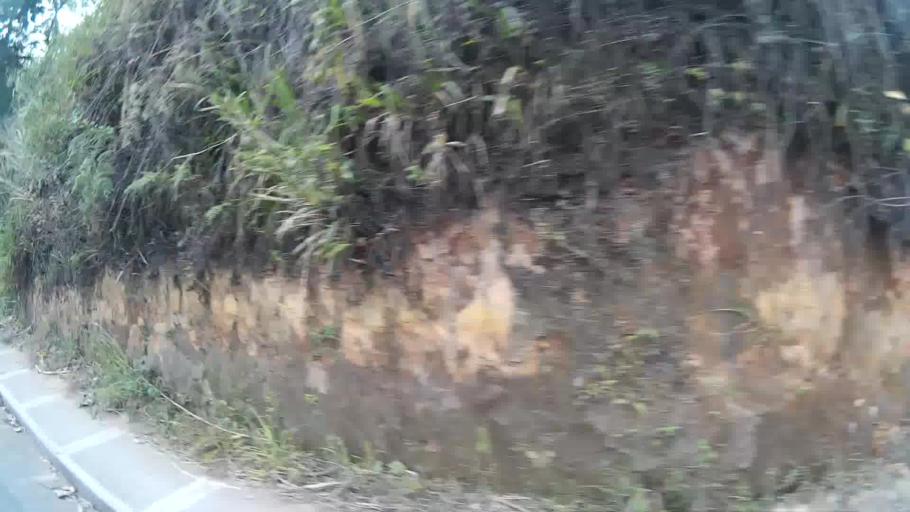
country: CO
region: Risaralda
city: Pereira
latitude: 4.8281
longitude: -75.7564
